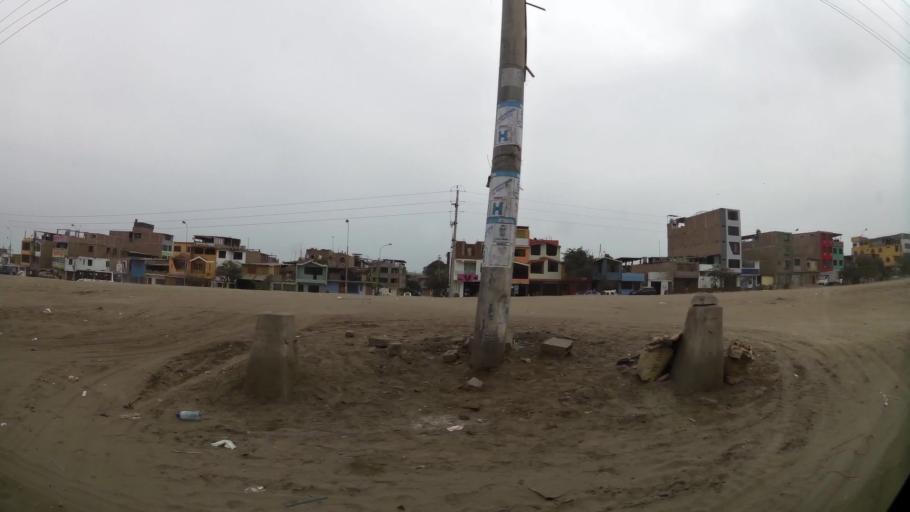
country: PE
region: Lima
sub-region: Lima
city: Surco
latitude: -12.2320
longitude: -76.9185
